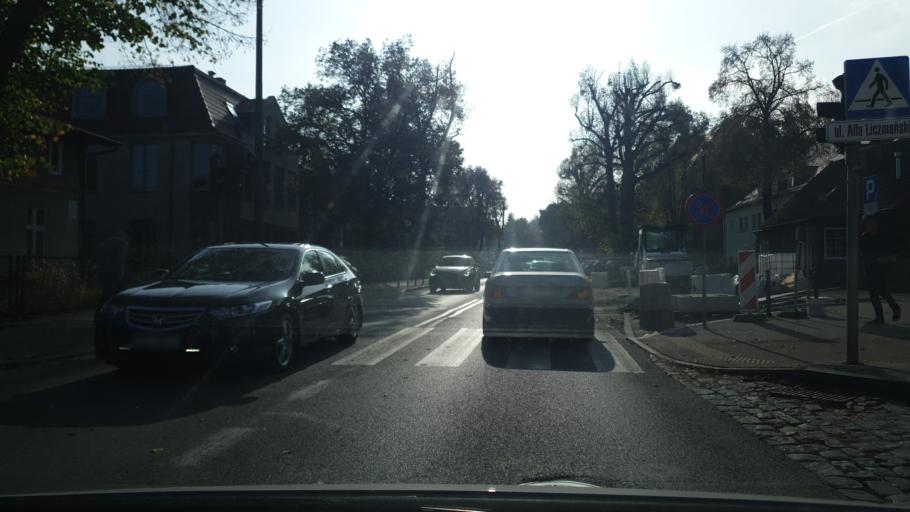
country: PL
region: Pomeranian Voivodeship
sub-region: Sopot
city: Sopot
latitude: 54.4080
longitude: 18.5593
